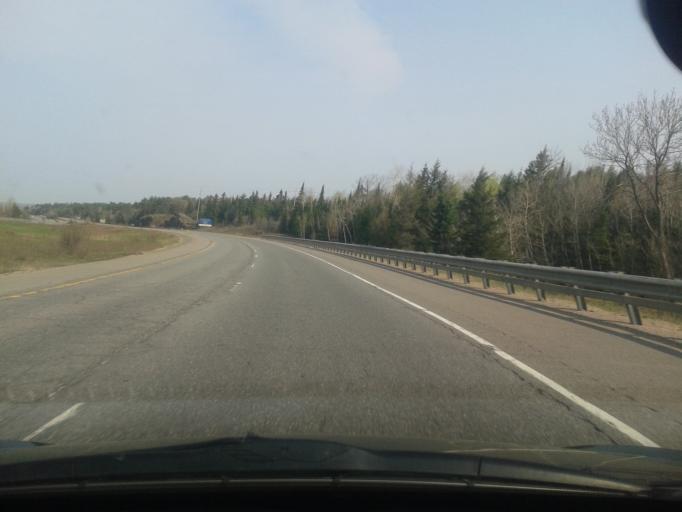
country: CA
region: Ontario
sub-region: Nipissing District
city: North Bay
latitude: 46.2773
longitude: -79.4017
